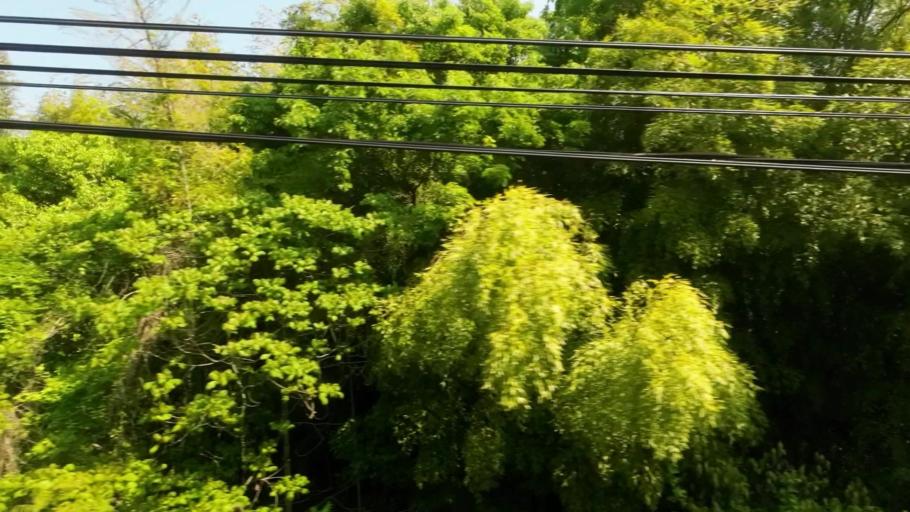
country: JP
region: Ehime
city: Saijo
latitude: 33.9225
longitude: 133.2329
